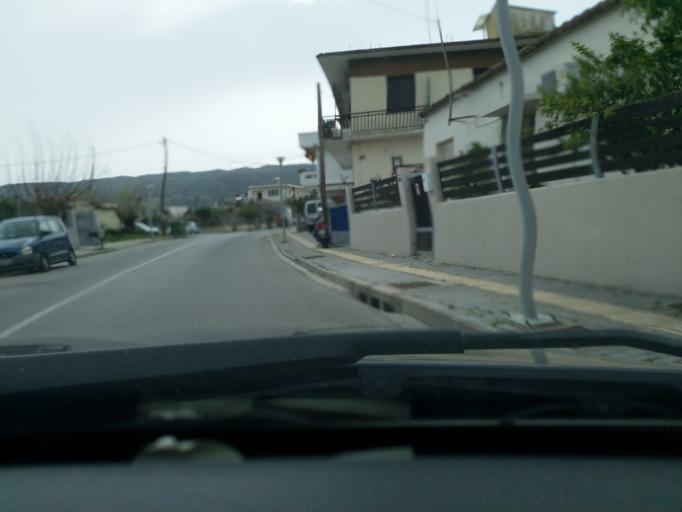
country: GR
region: Crete
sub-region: Nomos Chanias
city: Mournies
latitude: 35.4950
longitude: 24.0226
